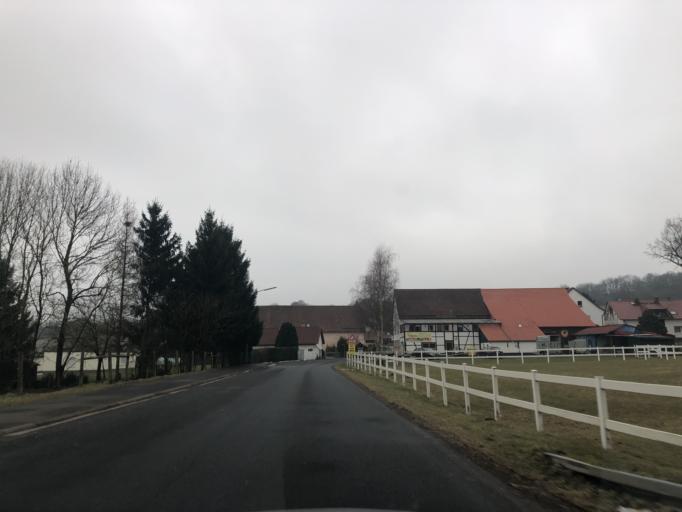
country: DE
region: Hesse
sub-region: Regierungsbezirk Darmstadt
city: Birstein
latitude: 50.4009
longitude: 9.2752
